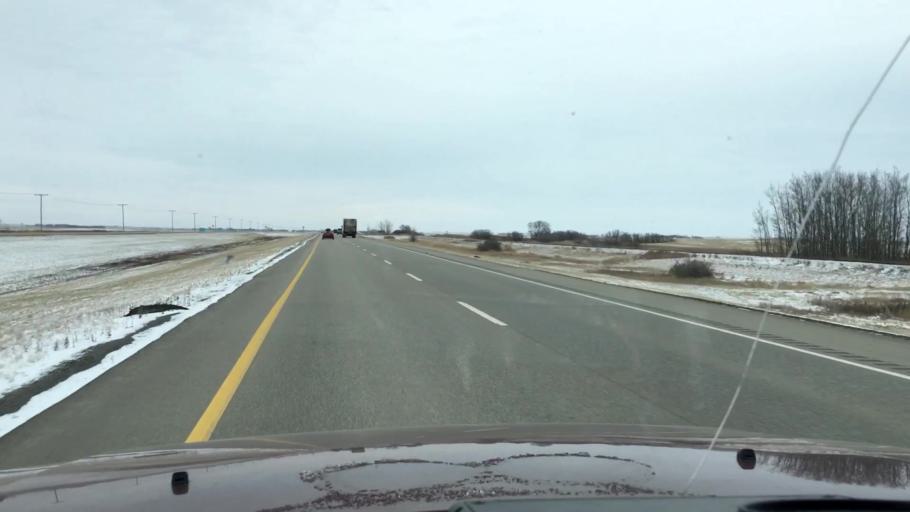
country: CA
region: Saskatchewan
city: Watrous
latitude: 51.1940
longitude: -105.9516
